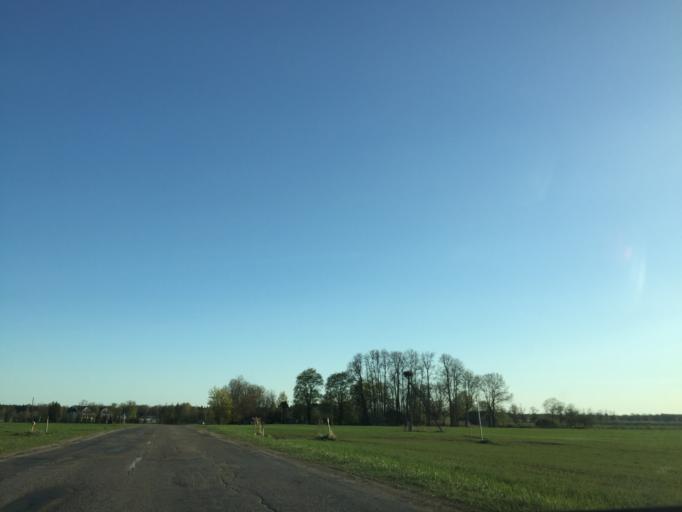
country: LV
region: Koknese
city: Koknese
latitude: 56.6828
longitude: 25.4865
